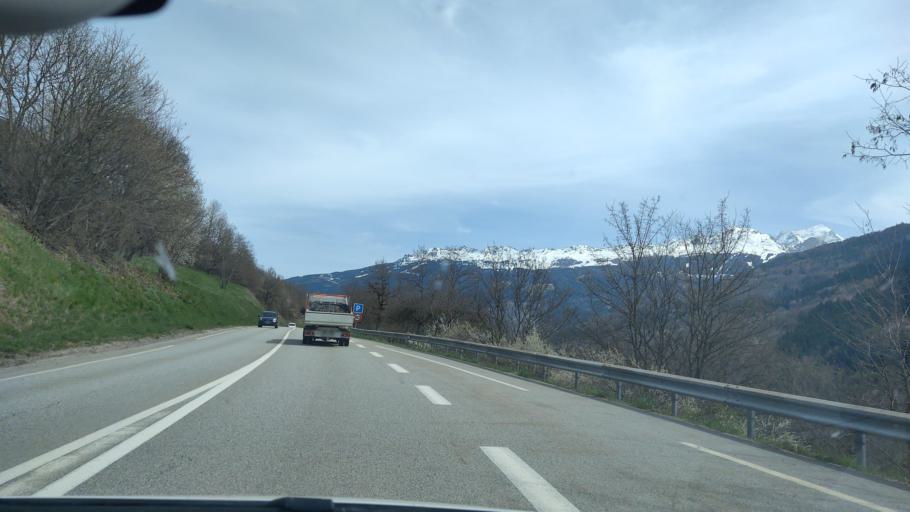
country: FR
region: Rhone-Alpes
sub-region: Departement de la Savoie
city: Macot-la-Plagne
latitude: 45.5646
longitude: 6.6901
